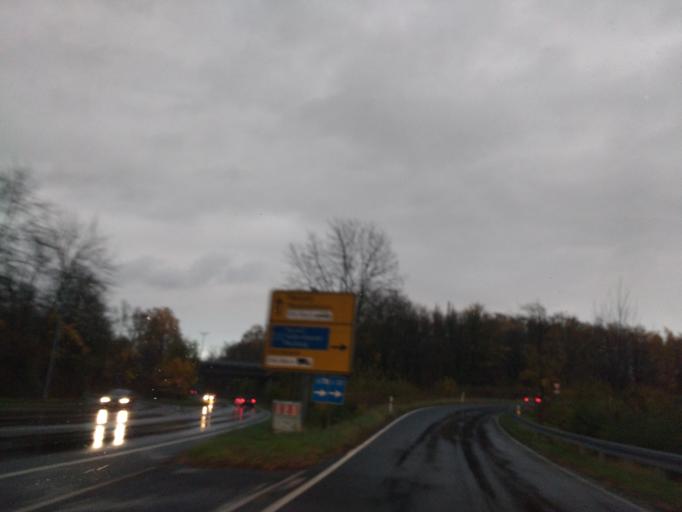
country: DE
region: Hesse
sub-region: Regierungsbezirk Kassel
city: Baunatal
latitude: 51.2578
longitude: 9.4202
